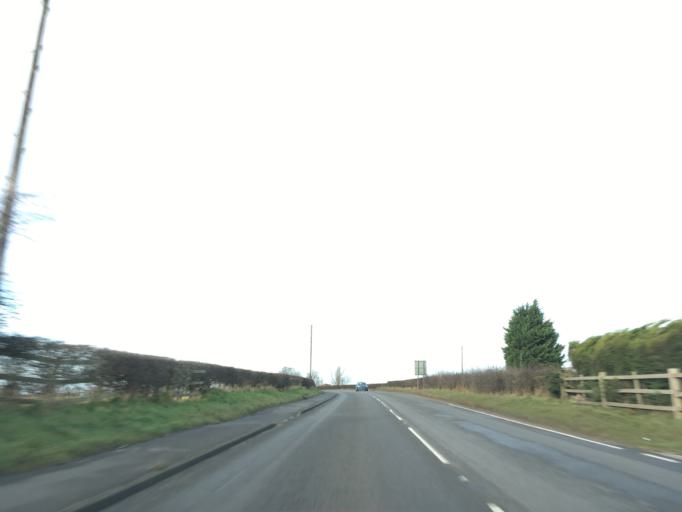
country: GB
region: England
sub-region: Nottinghamshire
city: South Collingham
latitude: 53.1602
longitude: -0.7618
